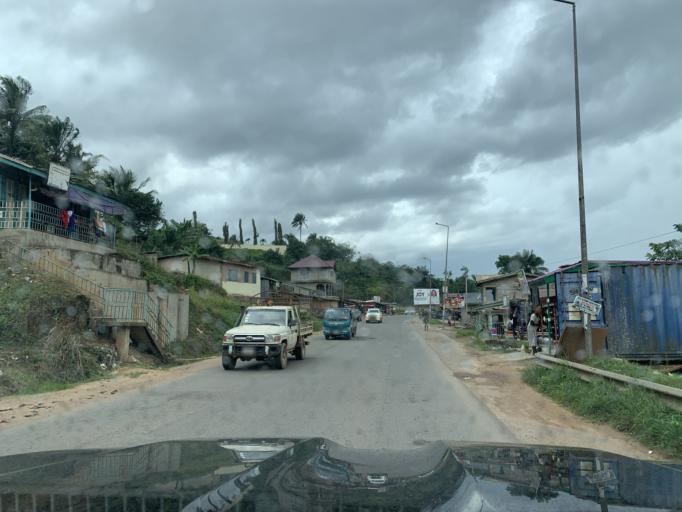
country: GH
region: Western
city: Tarkwa
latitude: 5.3140
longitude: -1.9905
